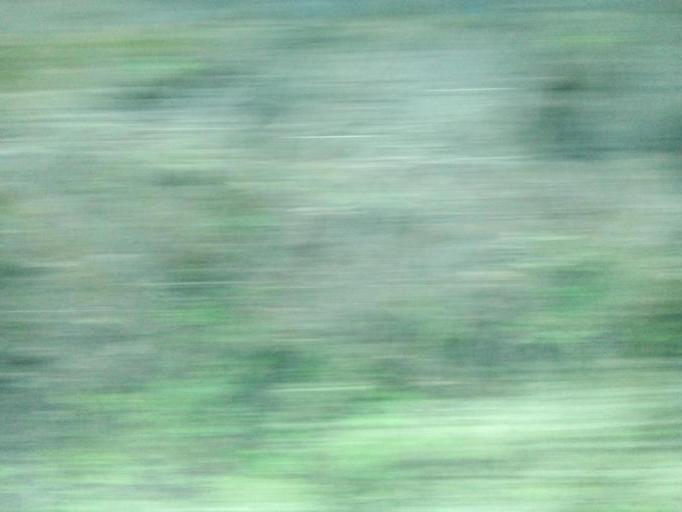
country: BR
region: Minas Gerais
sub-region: Belo Oriente
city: Belo Oriente
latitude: -19.2154
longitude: -42.2972
